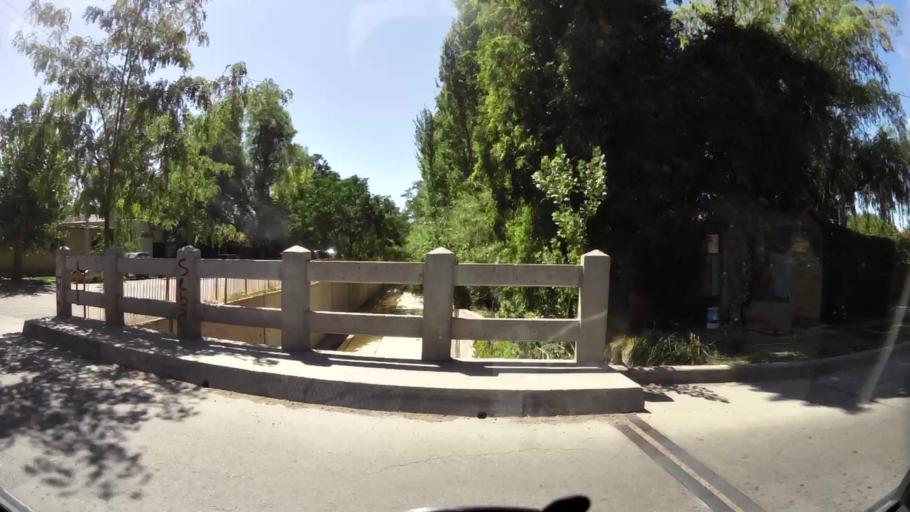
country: AR
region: Mendoza
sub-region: Departamento de Godoy Cruz
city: Godoy Cruz
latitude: -32.9644
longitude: -68.8668
